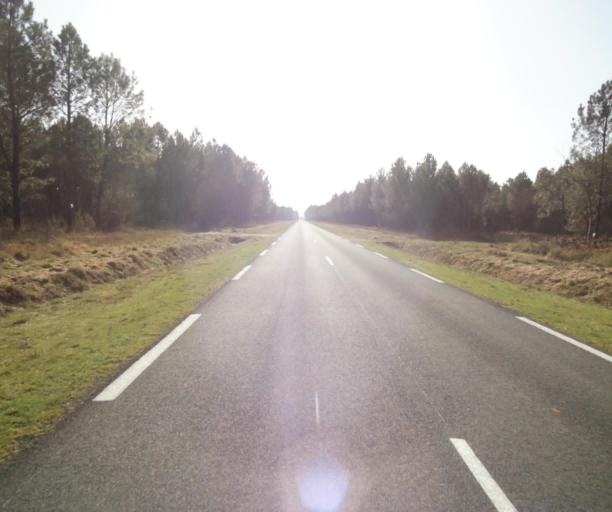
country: FR
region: Aquitaine
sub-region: Departement de la Gironde
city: Grignols
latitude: 44.1857
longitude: -0.1453
